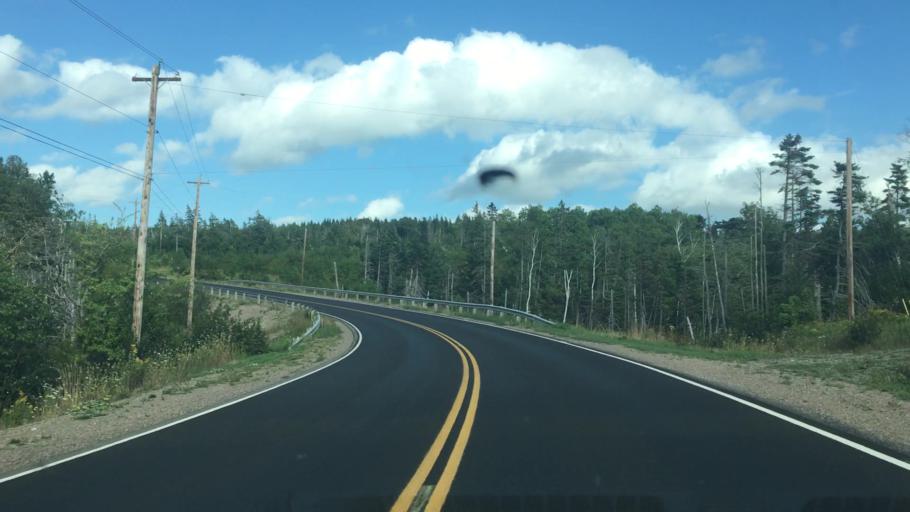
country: CA
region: Nova Scotia
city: Princeville
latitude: 45.8077
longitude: -60.7099
